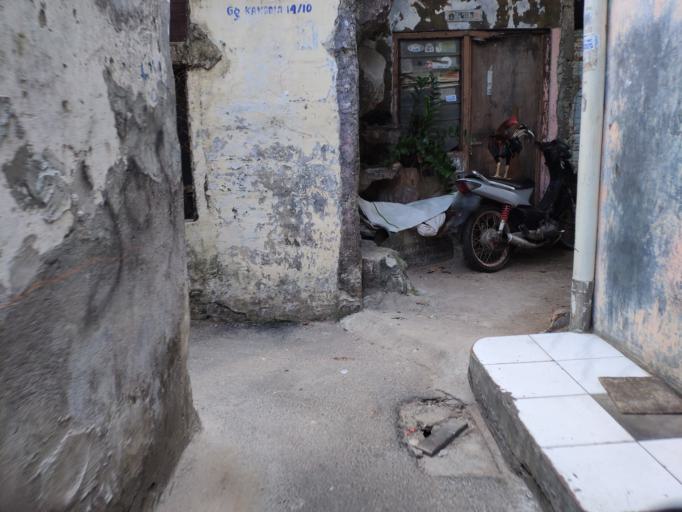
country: ID
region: Jakarta Raya
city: Jakarta
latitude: -6.1978
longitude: 106.8726
